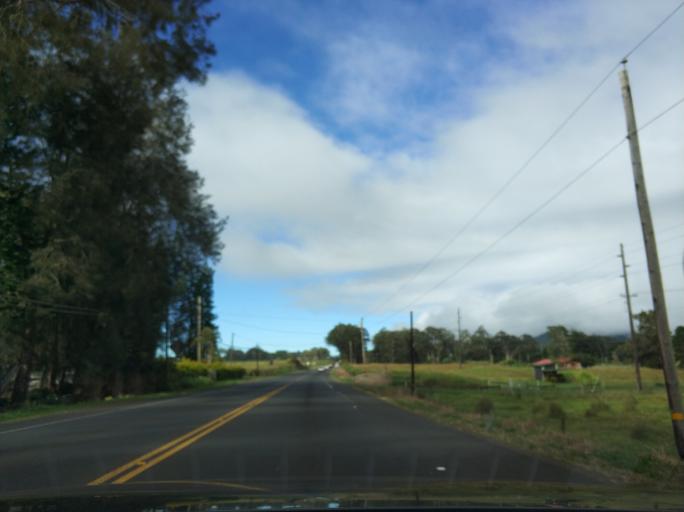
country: US
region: Hawaii
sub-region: Hawaii County
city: Waimea
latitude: 20.0425
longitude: -155.5981
